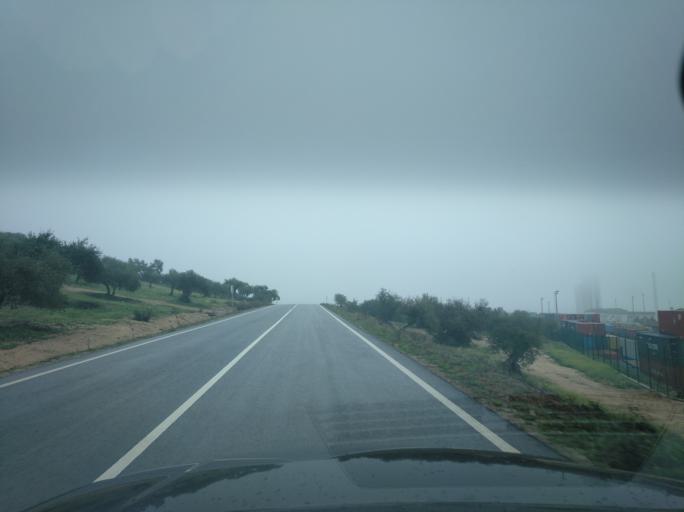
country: PT
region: Portalegre
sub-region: Elvas
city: Elvas
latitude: 38.8958
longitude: -7.1454
